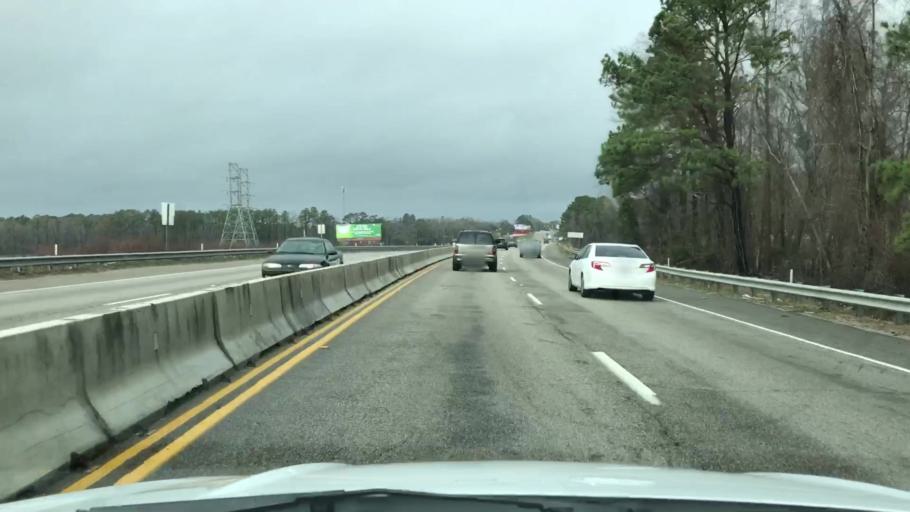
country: US
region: South Carolina
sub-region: Horry County
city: Conway
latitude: 33.8238
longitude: -79.0531
